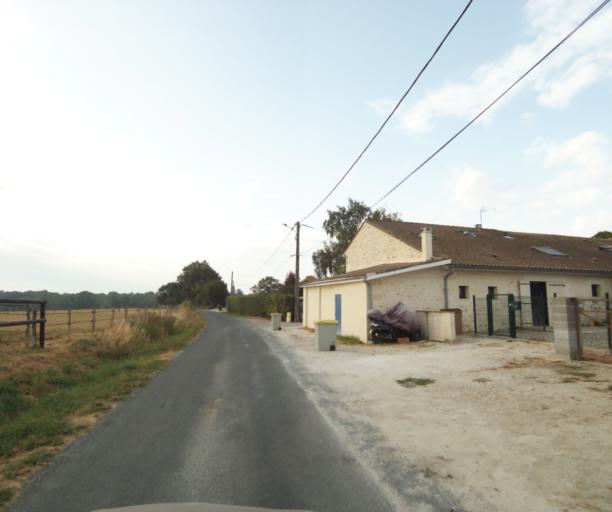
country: FR
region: Aquitaine
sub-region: Departement de la Gironde
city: Creon
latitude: 44.7769
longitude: -0.3391
